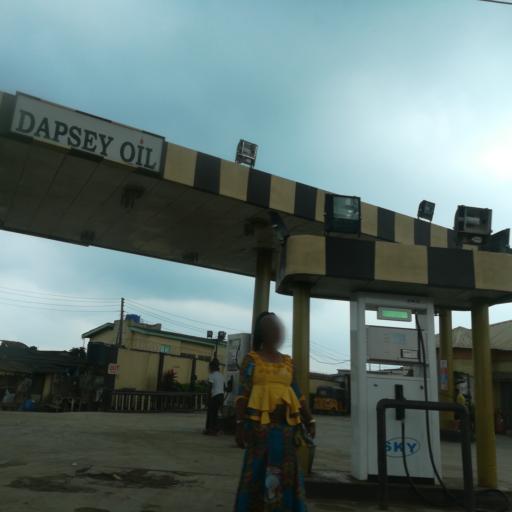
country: NG
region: Lagos
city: Agege
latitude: 6.5915
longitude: 3.3055
